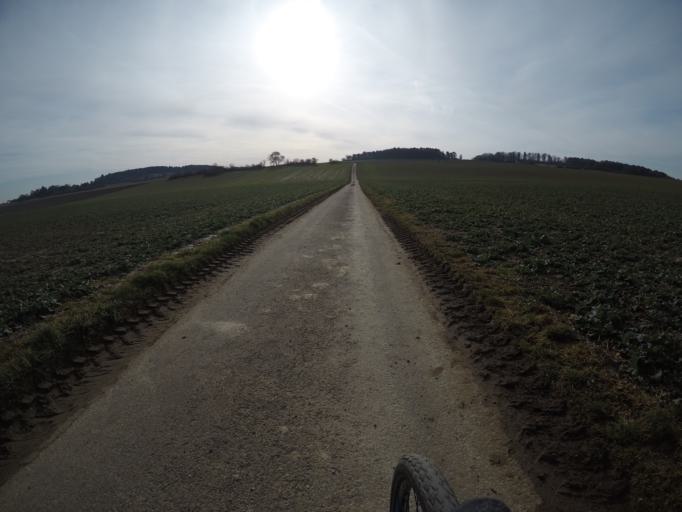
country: DE
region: Baden-Wuerttemberg
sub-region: Karlsruhe Region
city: Ostelsheim
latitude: 48.7031
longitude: 8.8656
